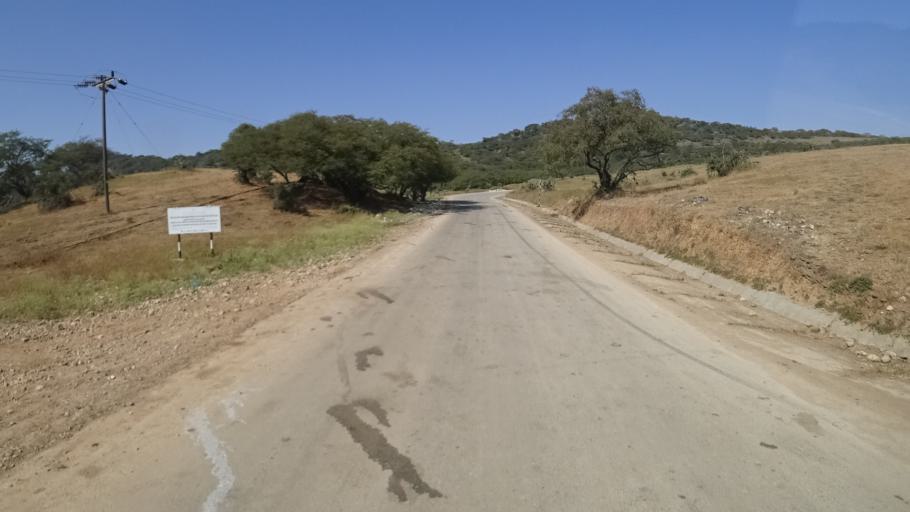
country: OM
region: Zufar
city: Salalah
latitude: 17.0671
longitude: 54.5978
